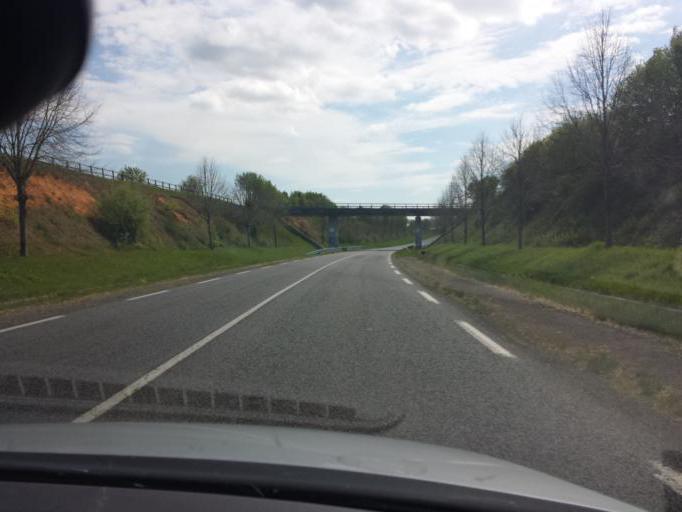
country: FR
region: Haute-Normandie
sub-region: Departement de l'Eure
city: Breteuil
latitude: 48.8352
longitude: 0.9379
